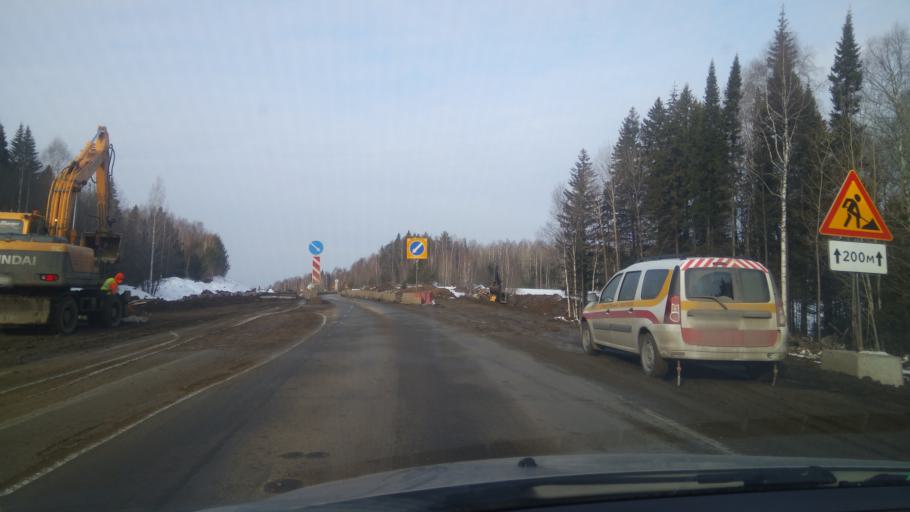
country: RU
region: Sverdlovsk
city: Bisert'
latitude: 56.8296
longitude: 59.1319
